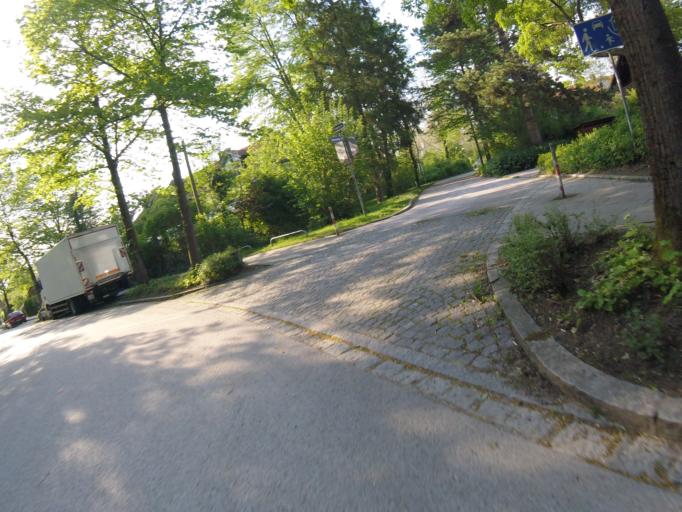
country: DE
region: Bavaria
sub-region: Upper Bavaria
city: Ottobrunn
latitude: 48.0551
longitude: 11.6602
